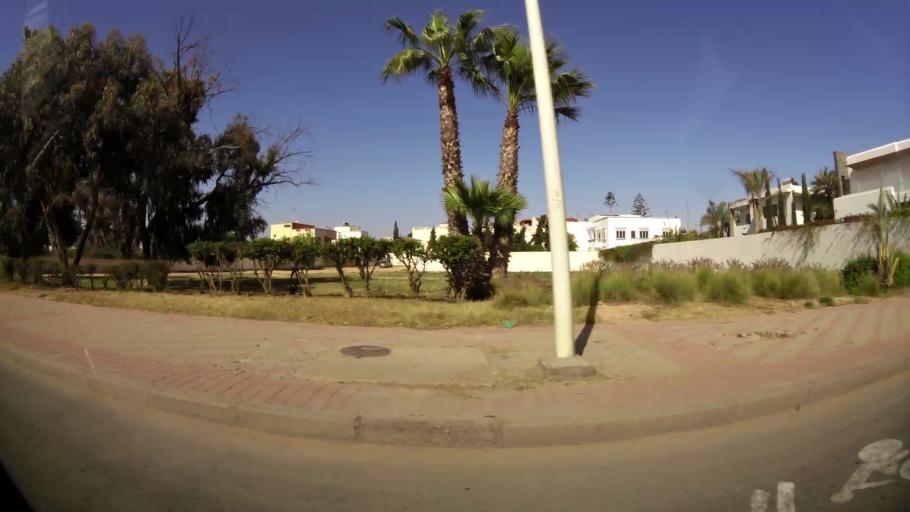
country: MA
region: Oued ed Dahab-Lagouira
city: Dakhla
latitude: 30.3922
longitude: -9.5774
